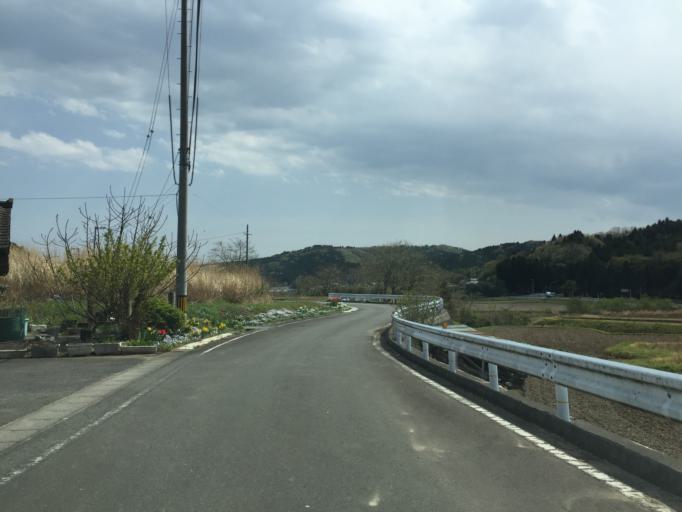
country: JP
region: Fukushima
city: Iwaki
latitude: 37.1665
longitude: 140.9730
